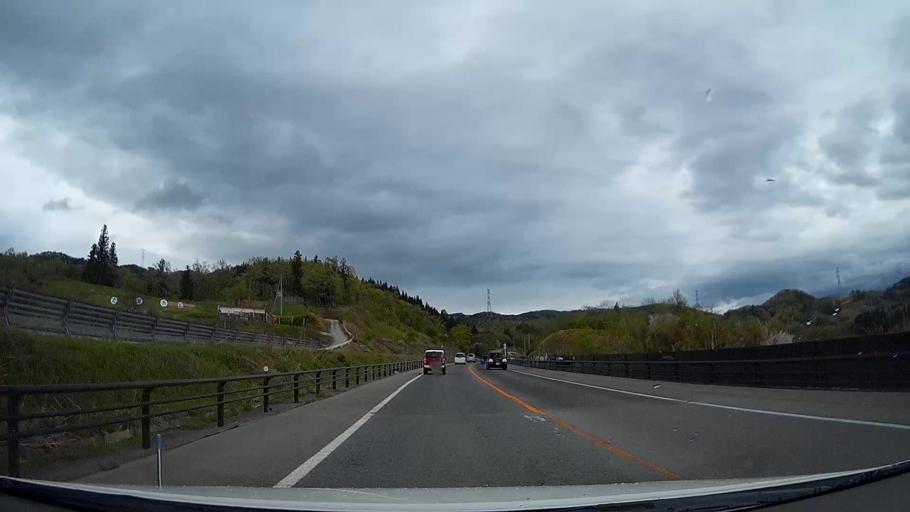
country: JP
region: Yamagata
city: Kaminoyama
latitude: 38.1216
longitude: 140.2117
